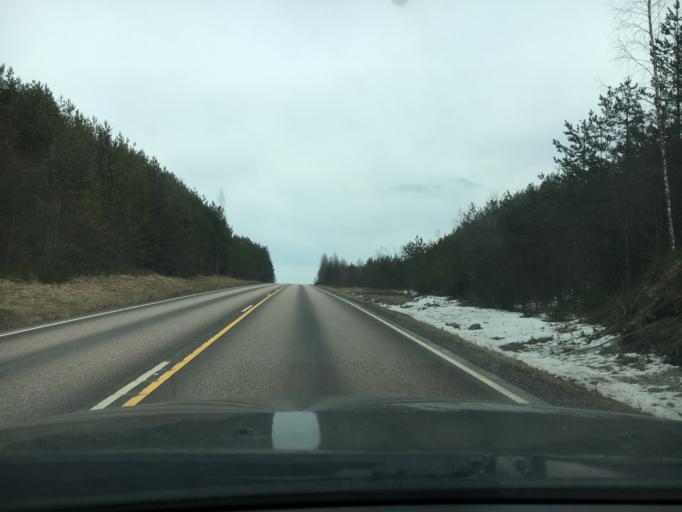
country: FI
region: Central Finland
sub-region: AEaenekoski
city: Konnevesi
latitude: 62.6871
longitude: 26.3958
